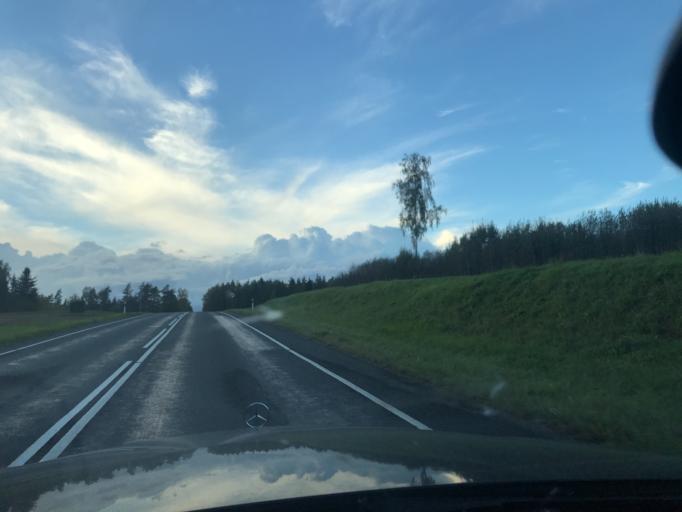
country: EE
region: Vorumaa
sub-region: Antsla vald
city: Vana-Antsla
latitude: 57.8715
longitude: 26.5952
